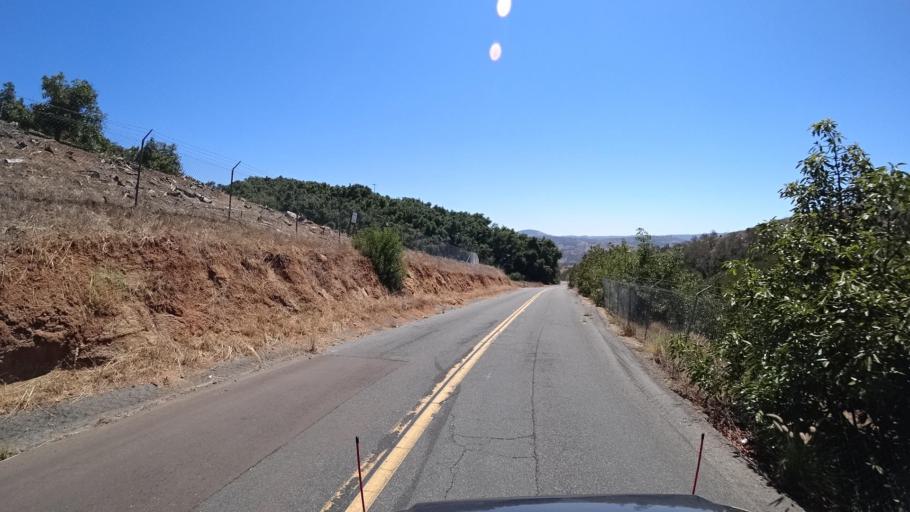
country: US
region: California
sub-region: San Diego County
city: Hidden Meadows
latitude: 33.3075
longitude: -117.0920
